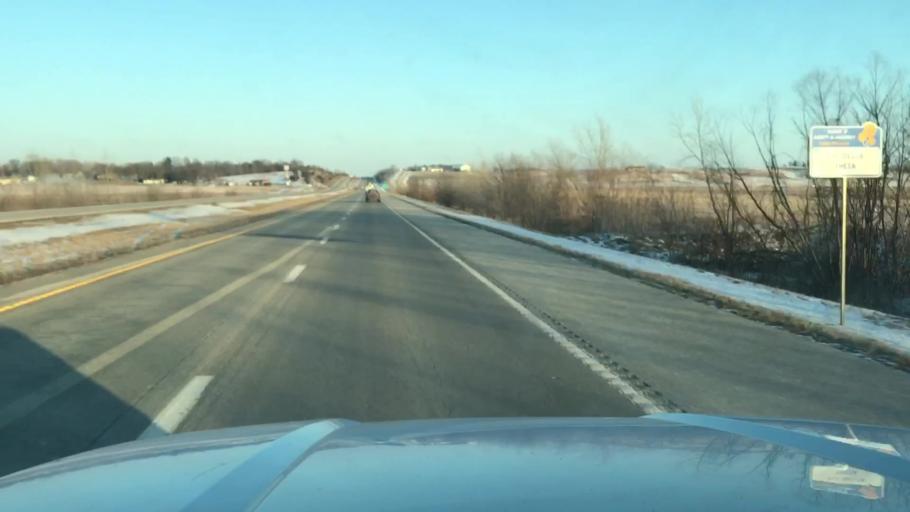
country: US
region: Missouri
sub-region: Buchanan County
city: Saint Joseph
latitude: 39.7477
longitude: -94.7210
